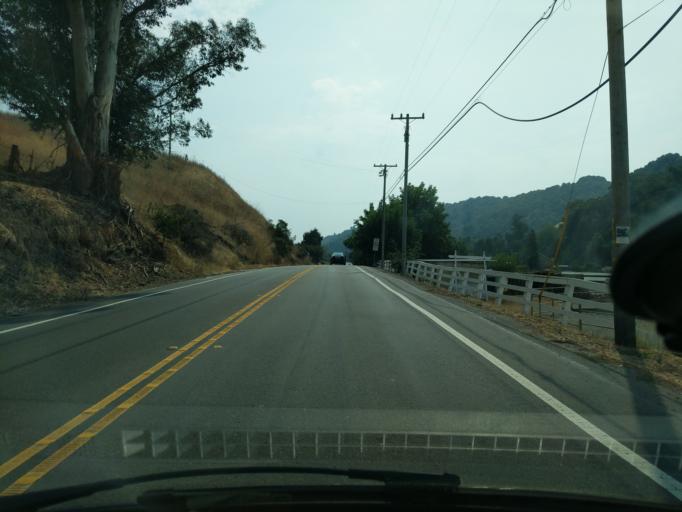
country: US
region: California
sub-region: Alameda County
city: Fairview
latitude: 37.7288
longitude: -122.0340
